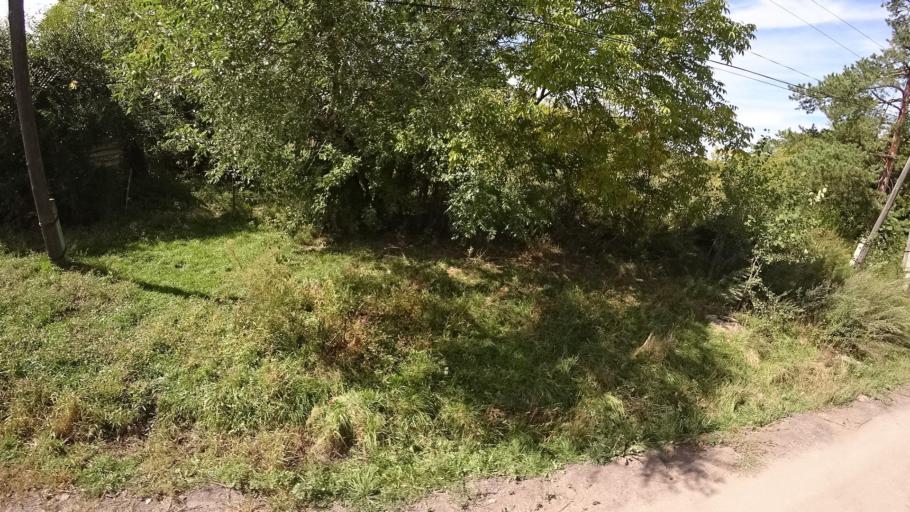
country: RU
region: Primorskiy
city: Yakovlevka
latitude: 44.4310
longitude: 133.5696
